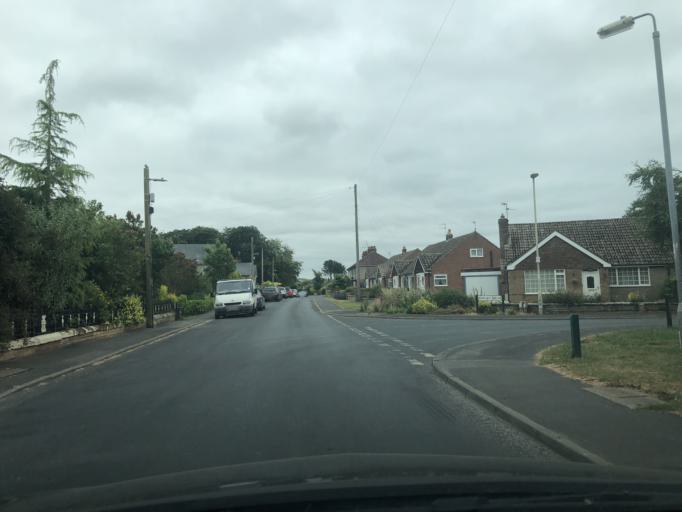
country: GB
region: England
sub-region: North Yorkshire
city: East Ayton
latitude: 54.2469
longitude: -0.4877
